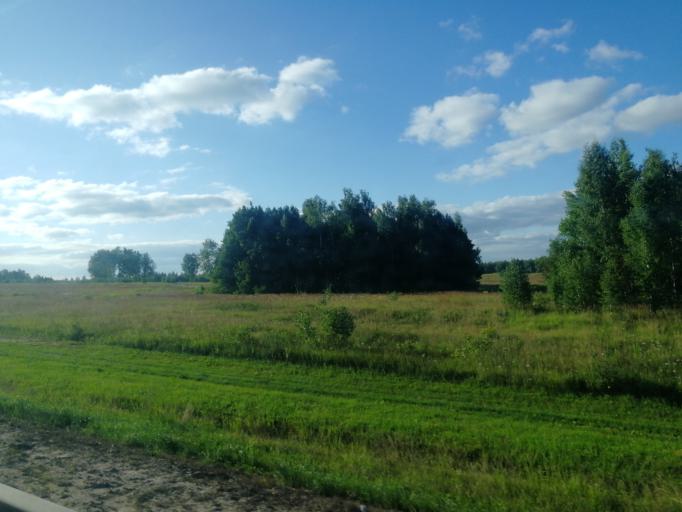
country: RU
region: Tula
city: Novogurovskiy
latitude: 54.2793
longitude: 37.2306
